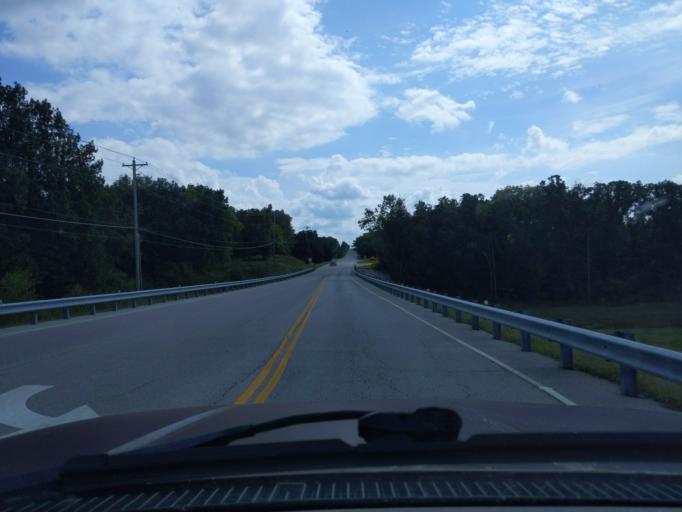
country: US
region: Oklahoma
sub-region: Tulsa County
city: Oakhurst
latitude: 36.0607
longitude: -96.0117
